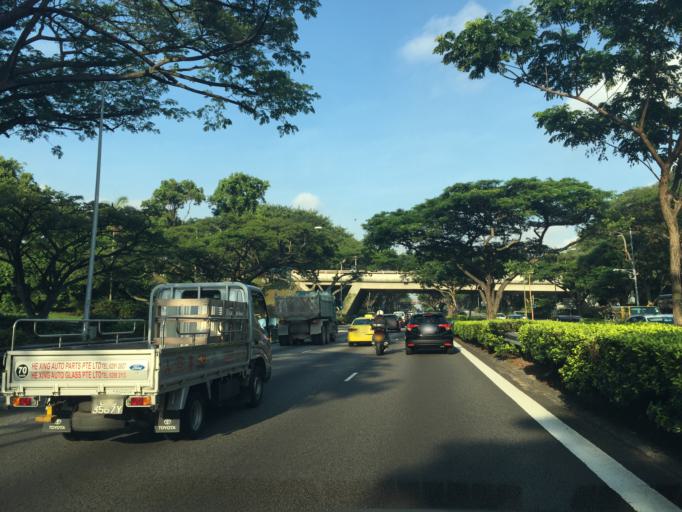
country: SG
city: Singapore
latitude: 1.3329
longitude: 103.9206
